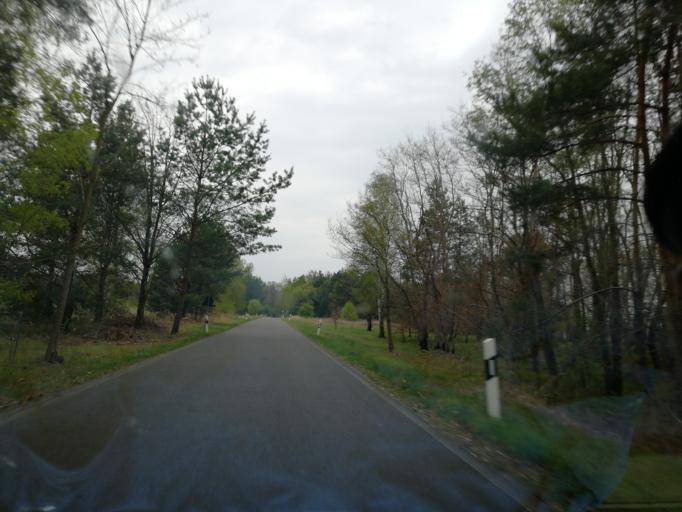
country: DE
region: Brandenburg
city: Calau
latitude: 51.7917
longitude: 13.8868
